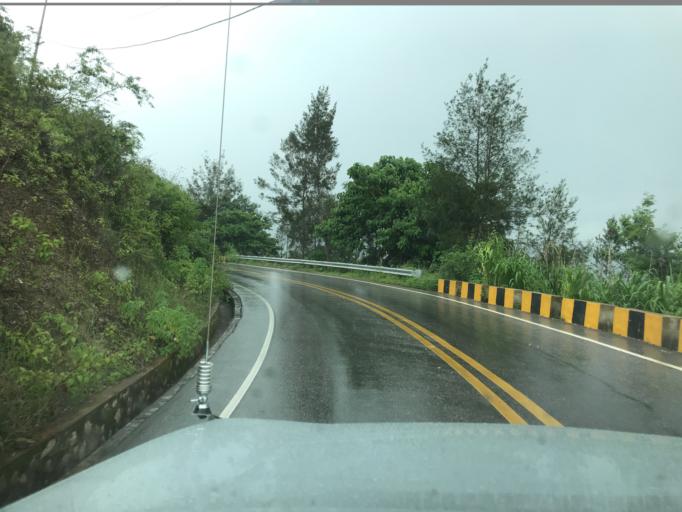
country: TL
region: Aileu
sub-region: Aileu Villa
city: Aileu
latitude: -8.8007
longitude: 125.5780
